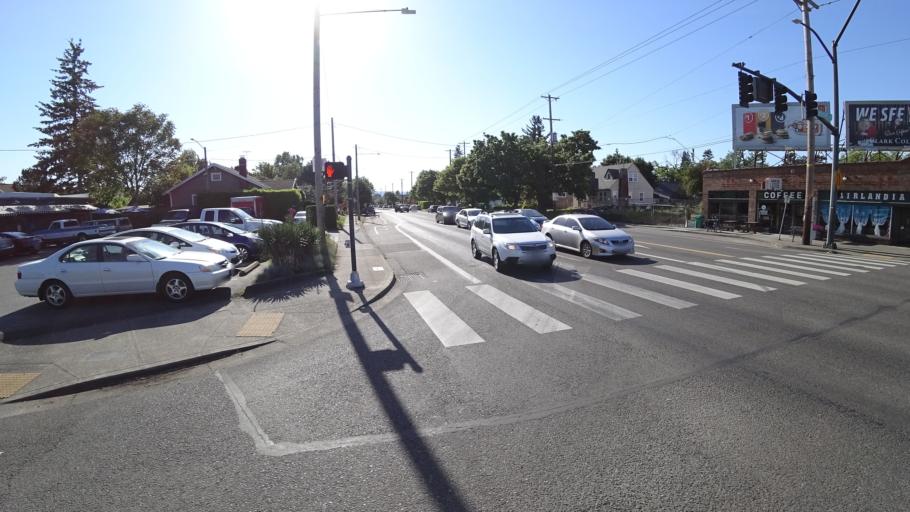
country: US
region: Oregon
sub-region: Multnomah County
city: Portland
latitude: 45.5698
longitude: -122.6823
